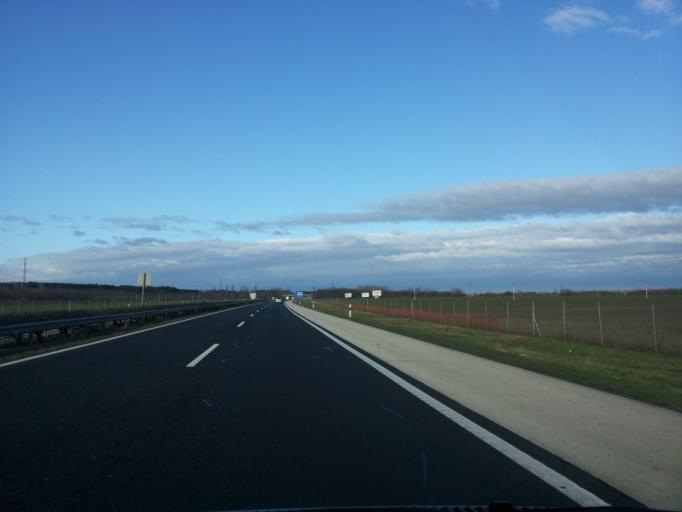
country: HU
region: Gyor-Moson-Sopron
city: Bony
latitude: 47.6847
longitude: 17.8316
